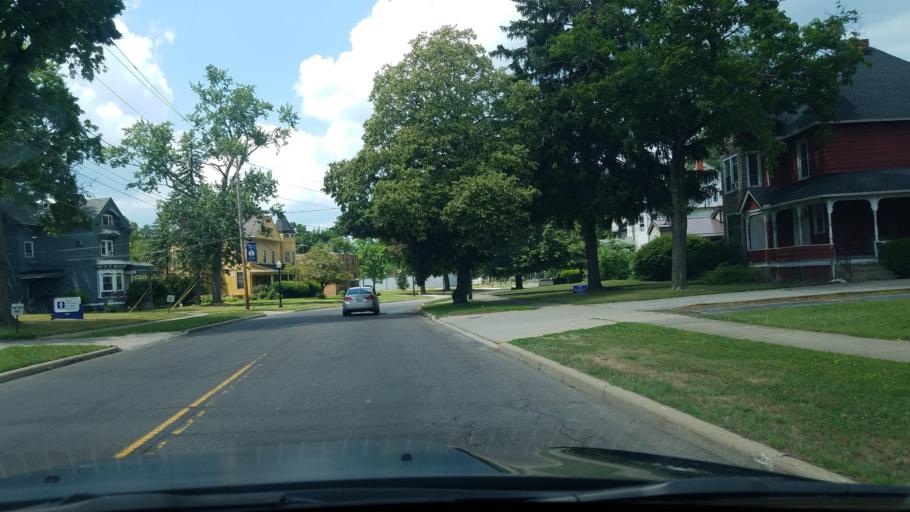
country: US
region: Ohio
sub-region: Trumbull County
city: Warren
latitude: 41.2408
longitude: -80.8240
